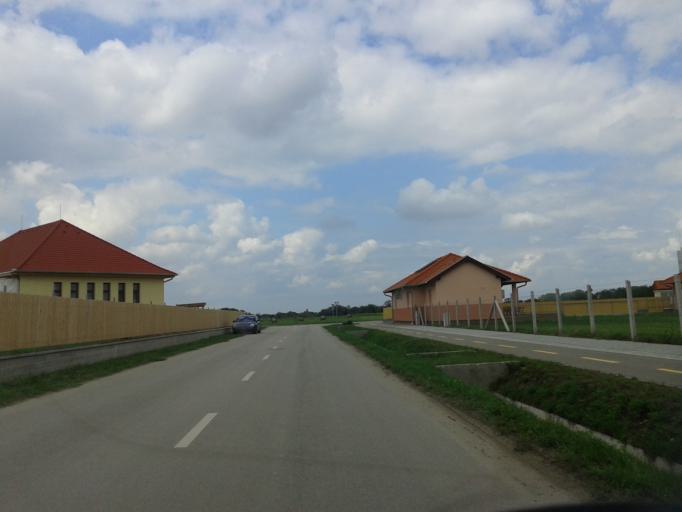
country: HU
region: Csongrad
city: Morahalom
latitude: 46.2216
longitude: 19.9038
